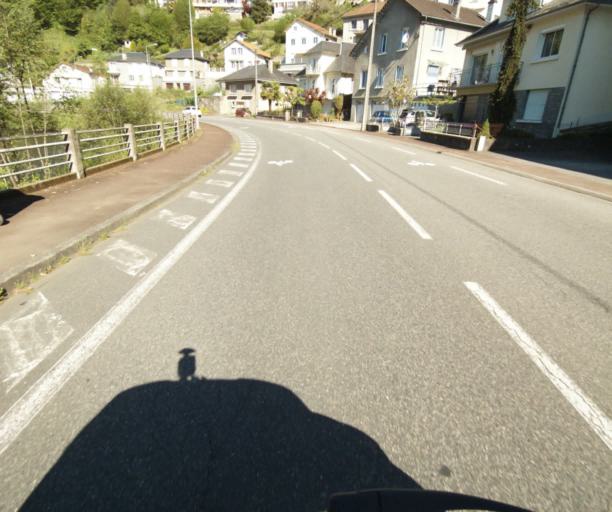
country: FR
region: Limousin
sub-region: Departement de la Correze
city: Tulle
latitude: 45.2768
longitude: 1.7755
